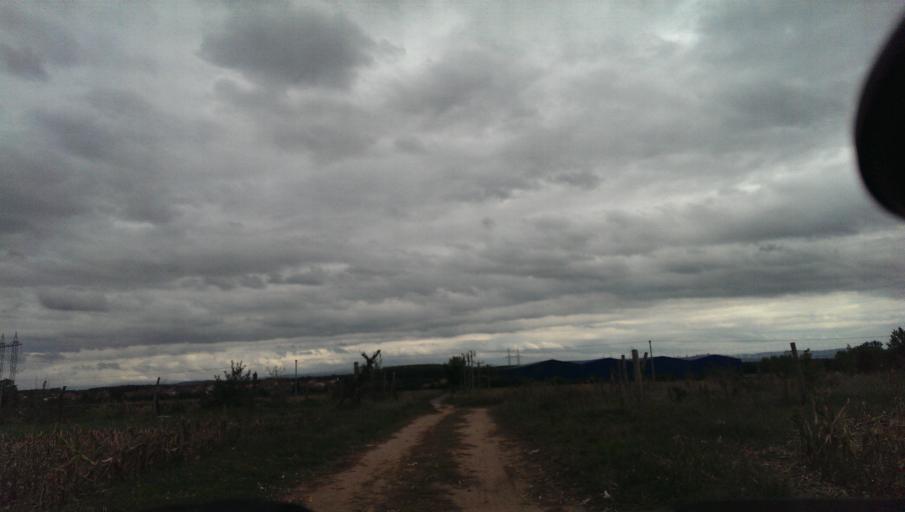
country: CZ
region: South Moravian
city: Moravsky Pisek
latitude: 48.9879
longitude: 17.3170
